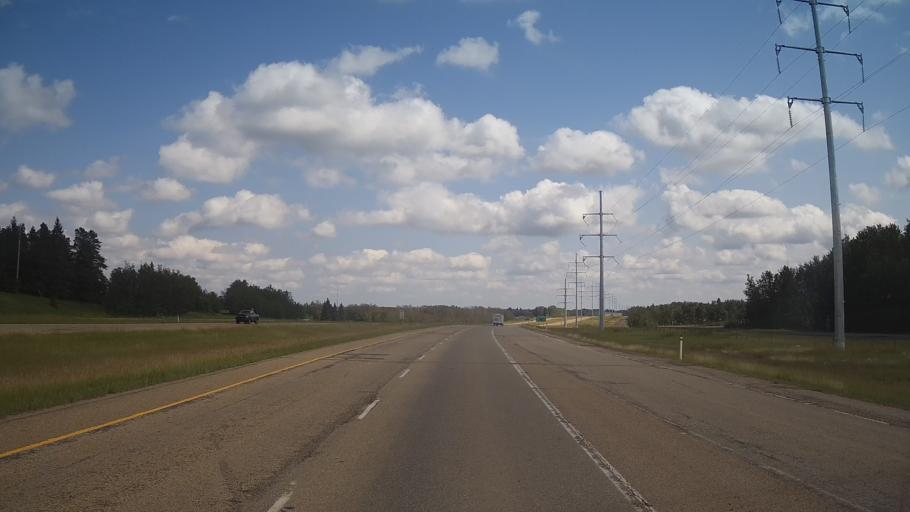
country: CA
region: Alberta
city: Sherwood Park
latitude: 53.4463
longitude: -113.2414
